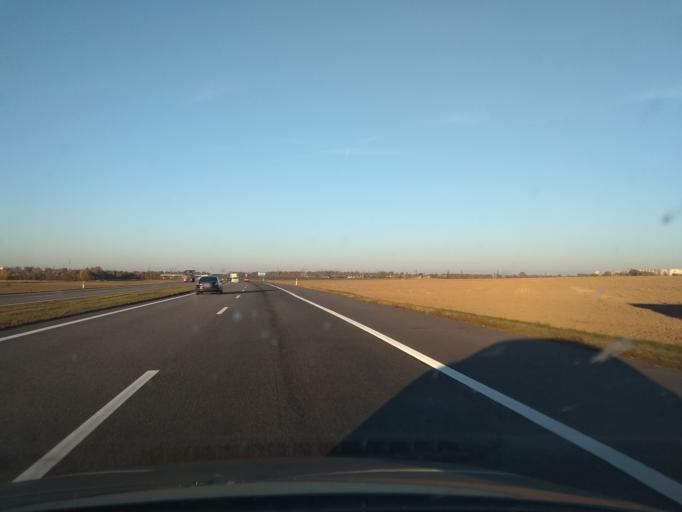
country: BY
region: Brest
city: Baranovichi
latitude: 53.1523
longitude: 25.9728
